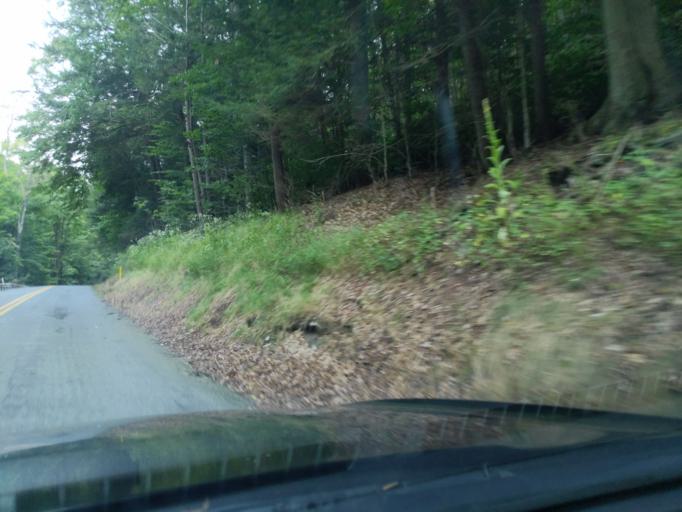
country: US
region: Pennsylvania
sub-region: Cambria County
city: Portage
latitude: 40.3256
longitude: -78.5766
